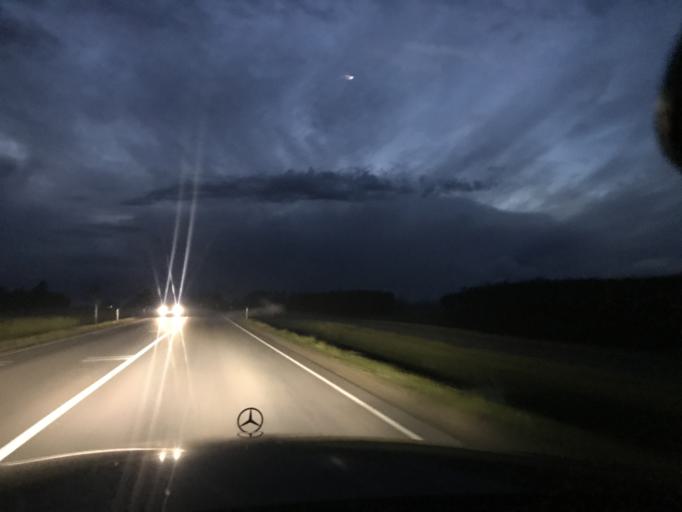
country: EE
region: Valgamaa
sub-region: Torva linn
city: Torva
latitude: 58.0077
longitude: 25.9112
